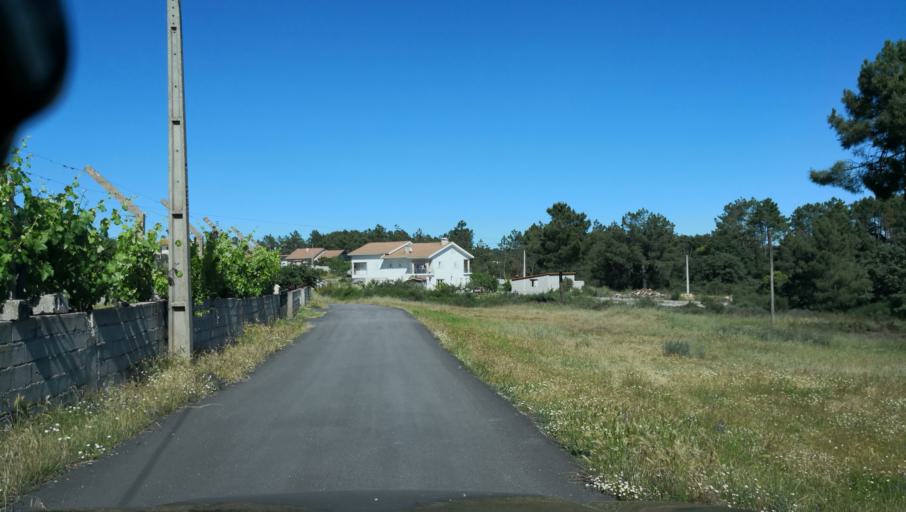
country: PT
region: Vila Real
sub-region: Vila Real
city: Vila Real
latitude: 41.2993
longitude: -7.6740
